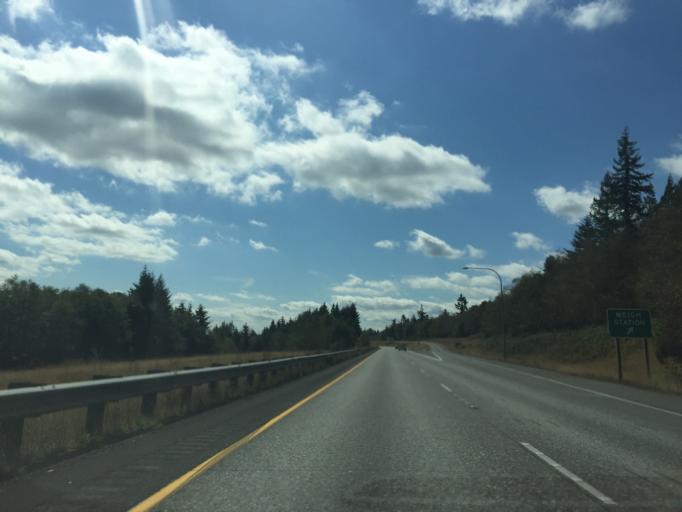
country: US
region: Washington
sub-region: Skagit County
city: Burlington
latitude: 48.5468
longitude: -122.3505
